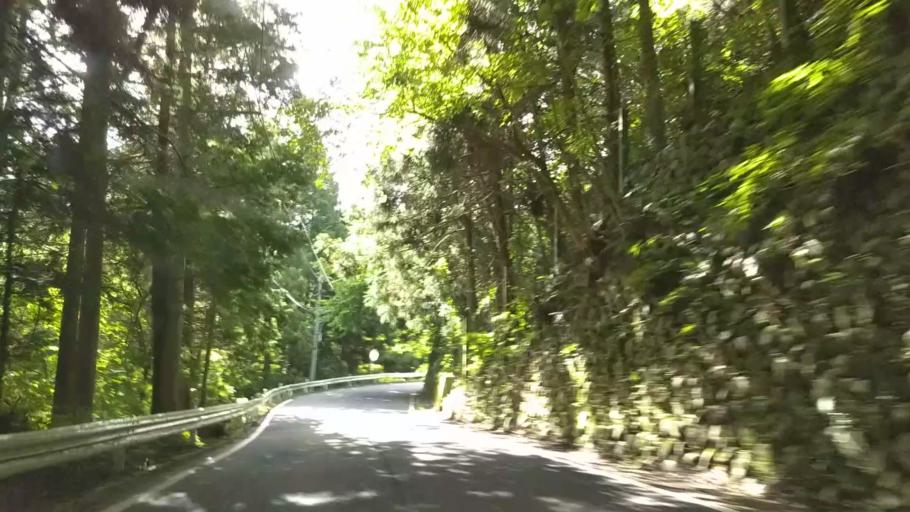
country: JP
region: Yamanashi
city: Uenohara
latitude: 35.5636
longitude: 139.1465
